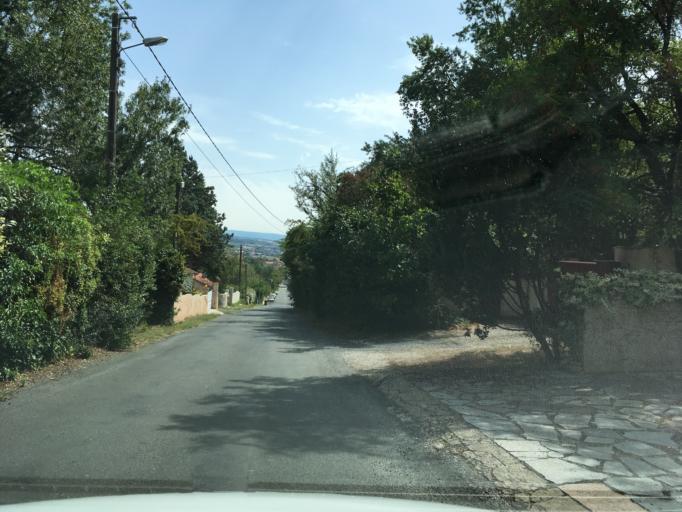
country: FR
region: Midi-Pyrenees
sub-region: Departement du Tarn
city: Castres
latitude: 43.6115
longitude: 2.2221
